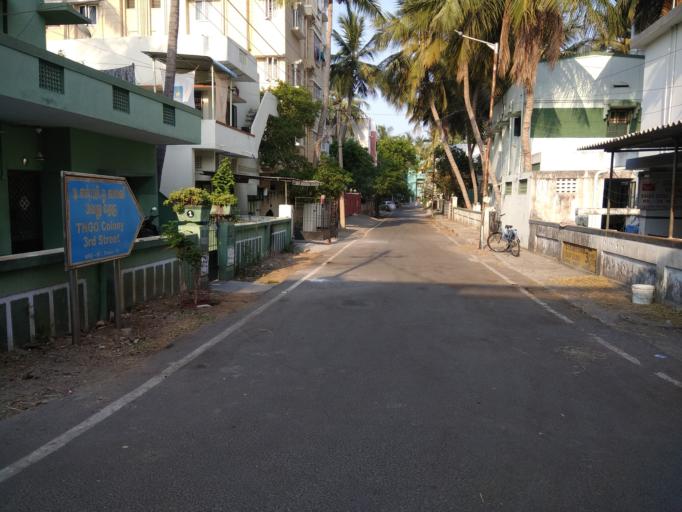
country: IN
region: Tamil Nadu
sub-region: Kancheepuram
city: Madipakkam
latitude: 12.9803
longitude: 80.1865
